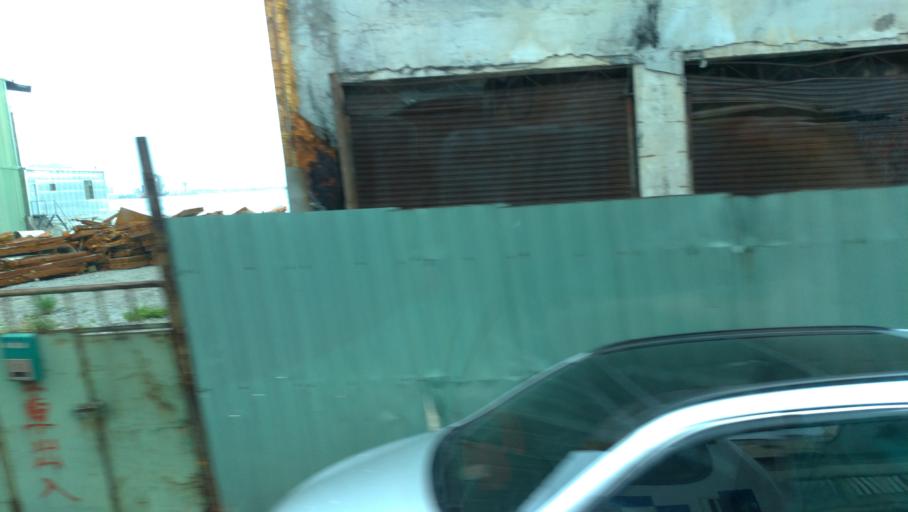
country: TW
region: Taiwan
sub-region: Keelung
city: Keelung
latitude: 25.1496
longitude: 121.7642
